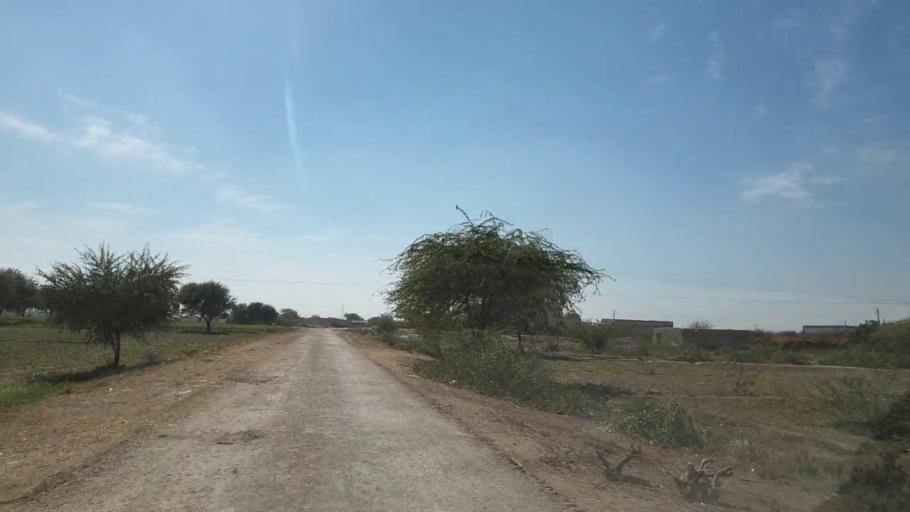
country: PK
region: Sindh
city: Pithoro
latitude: 25.6328
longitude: 69.2507
